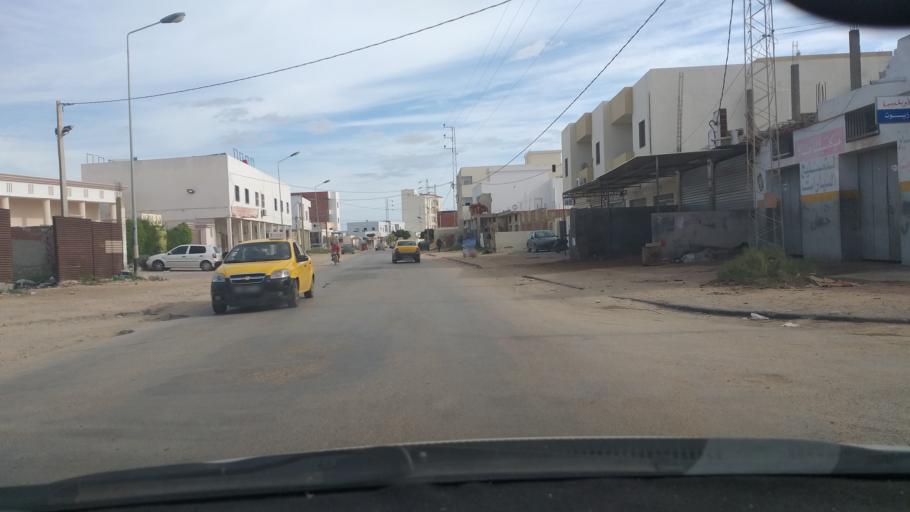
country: TN
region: Safaqis
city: Al Qarmadah
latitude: 34.7986
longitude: 10.7970
